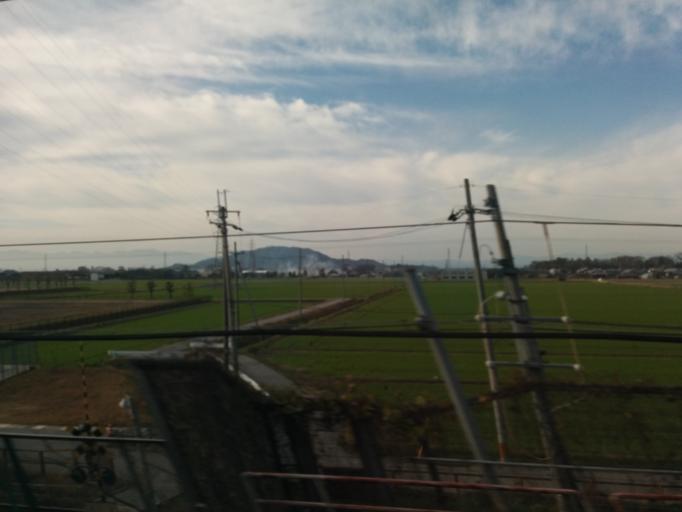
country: JP
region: Shiga Prefecture
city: Hikone
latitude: 35.2178
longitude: 136.2501
